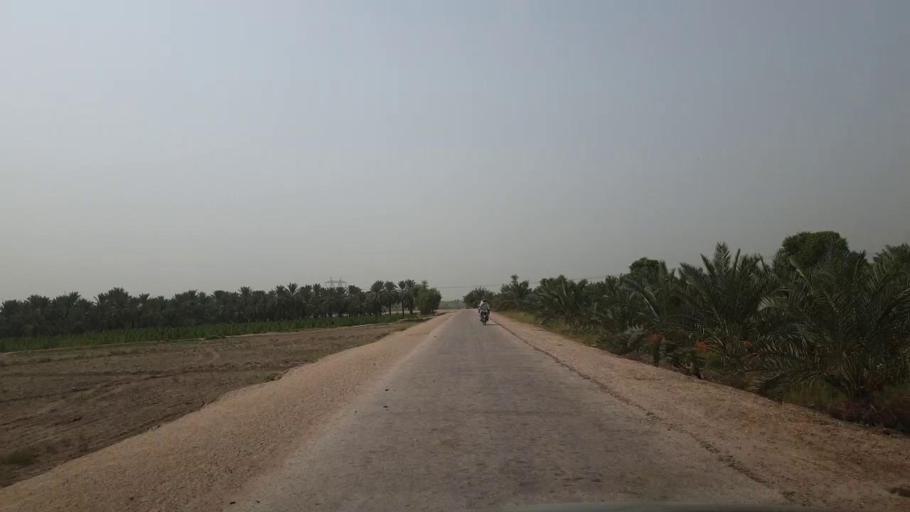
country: PK
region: Sindh
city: Gambat
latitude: 27.4186
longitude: 68.5480
